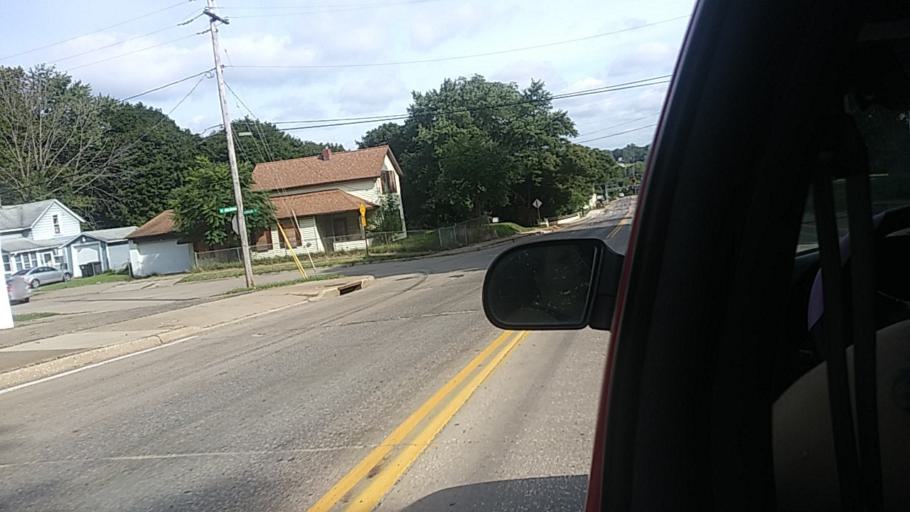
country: US
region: Ohio
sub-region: Summit County
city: Akron
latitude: 41.0826
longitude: -81.4904
